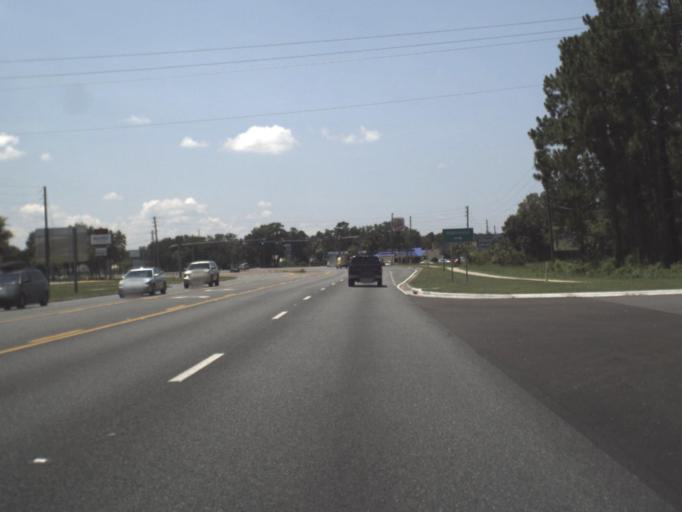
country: US
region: Florida
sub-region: Citrus County
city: Homosassa Springs
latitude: 28.8002
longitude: -82.5765
